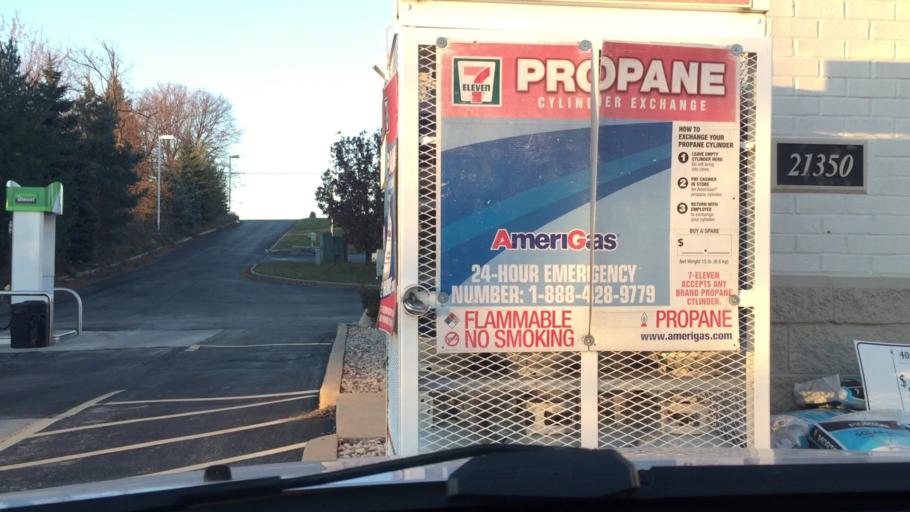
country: US
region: Wisconsin
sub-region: Waukesha County
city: Lannon
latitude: 43.0840
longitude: -88.1783
